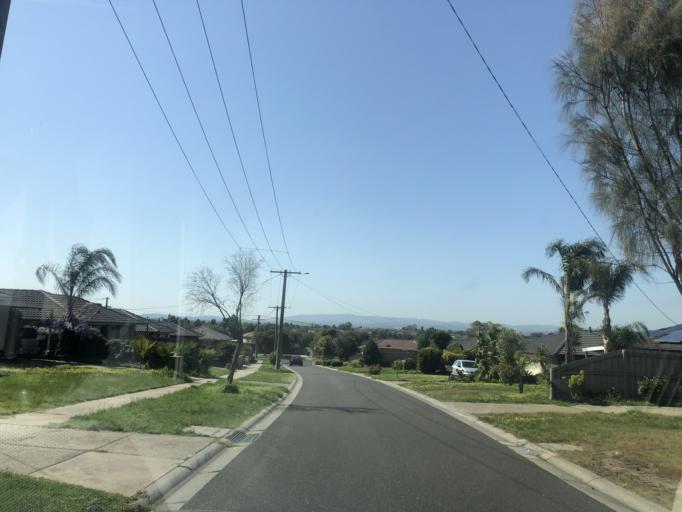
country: AU
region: Victoria
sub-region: Casey
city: Narre Warren South
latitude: -38.0421
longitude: 145.2721
